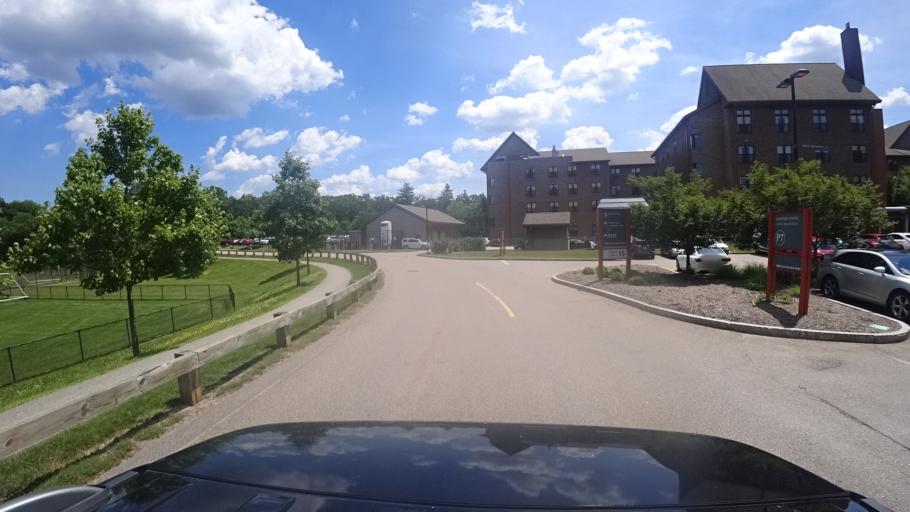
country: US
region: Massachusetts
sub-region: Norfolk County
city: Dedham
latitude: 42.2673
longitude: -71.1938
